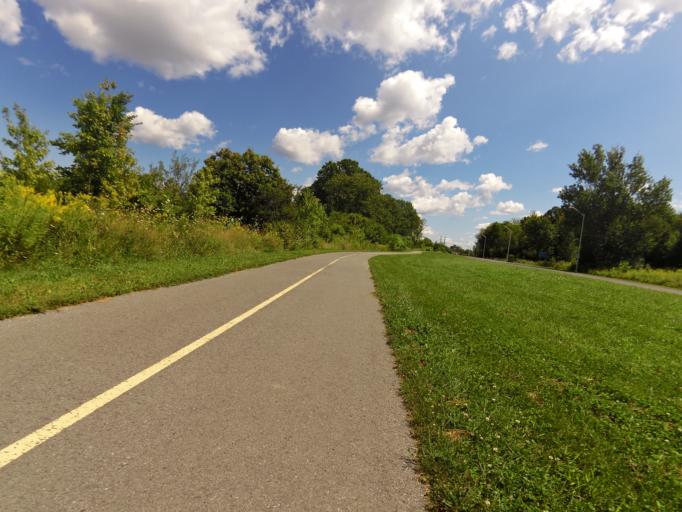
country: CA
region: Ontario
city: Ottawa
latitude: 45.3712
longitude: -75.6752
